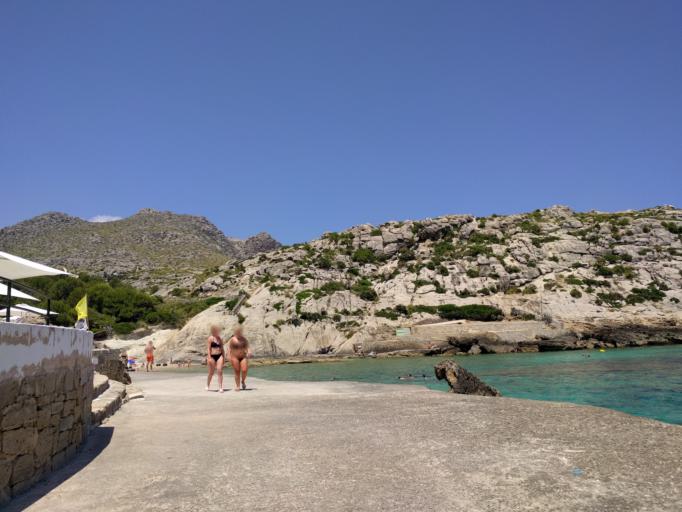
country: ES
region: Balearic Islands
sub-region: Illes Balears
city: Pollenca
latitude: 39.9213
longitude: 3.0559
